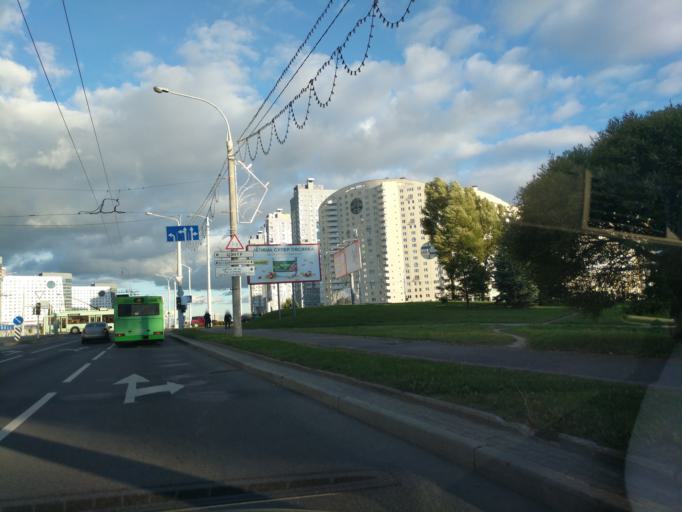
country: BY
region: Minsk
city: Novoye Medvezhino
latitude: 53.8576
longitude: 27.4765
